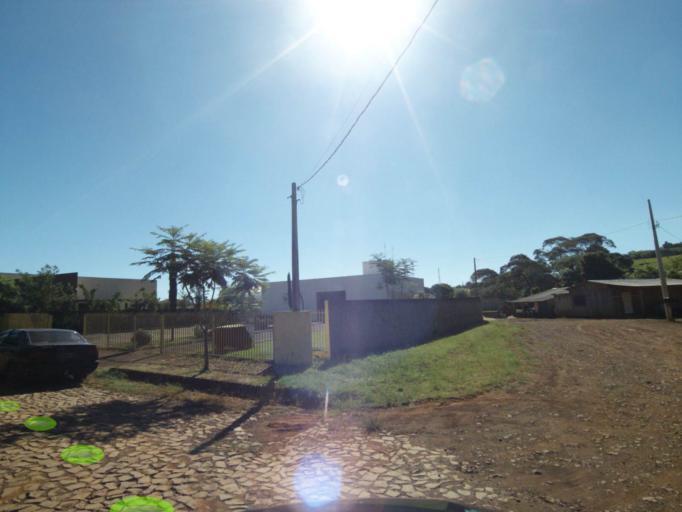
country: BR
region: Parana
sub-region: Coronel Vivida
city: Coronel Vivida
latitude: -26.1425
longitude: -52.3785
